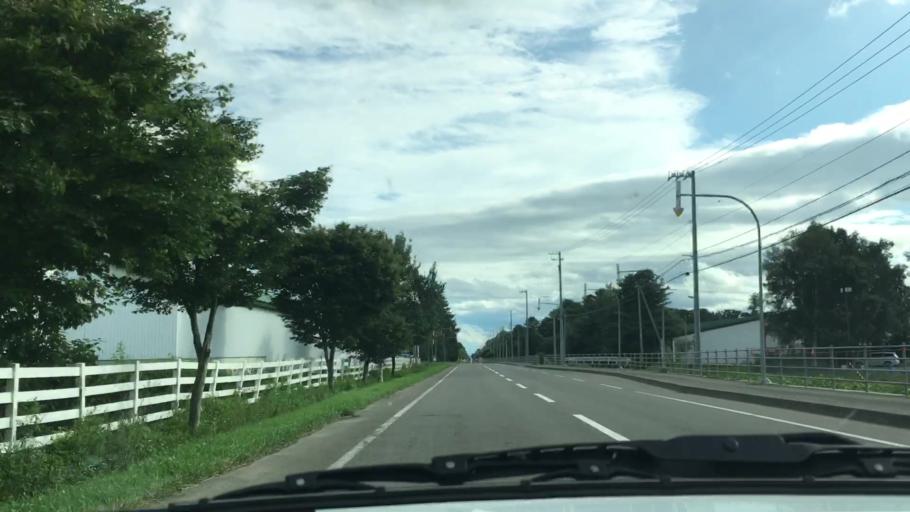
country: JP
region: Hokkaido
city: Otofuke
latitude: 43.2506
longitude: 143.2991
